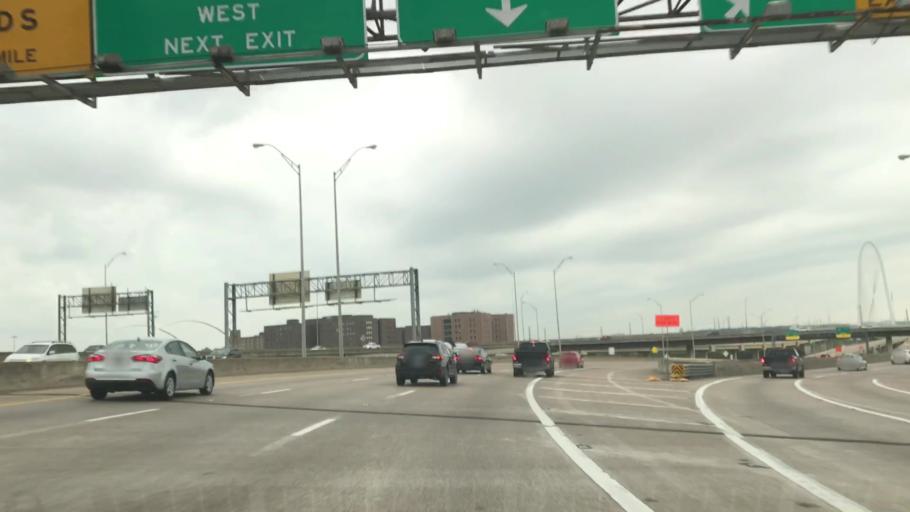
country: US
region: Texas
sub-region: Dallas County
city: Dallas
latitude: 32.7831
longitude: -96.8090
